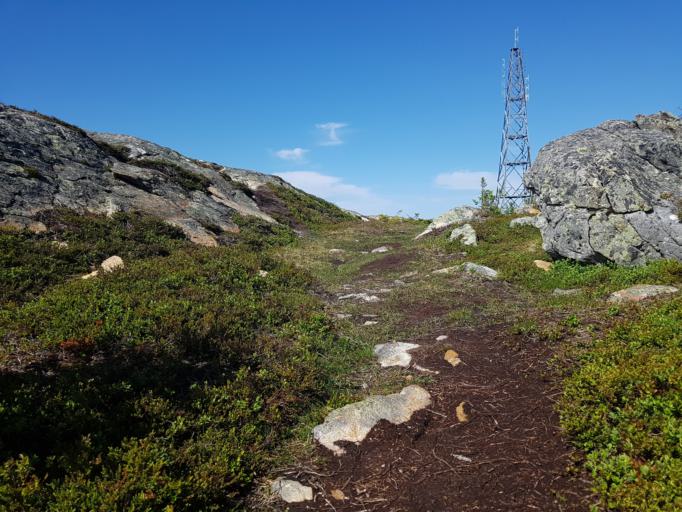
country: NO
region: Sor-Trondelag
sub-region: Melhus
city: Melhus
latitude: 63.4202
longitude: 10.2506
